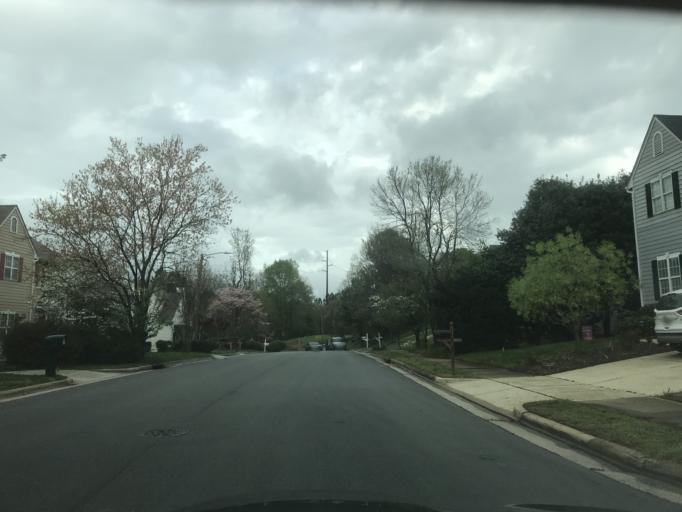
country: US
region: North Carolina
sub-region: Wake County
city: West Raleigh
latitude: 35.7485
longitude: -78.6855
